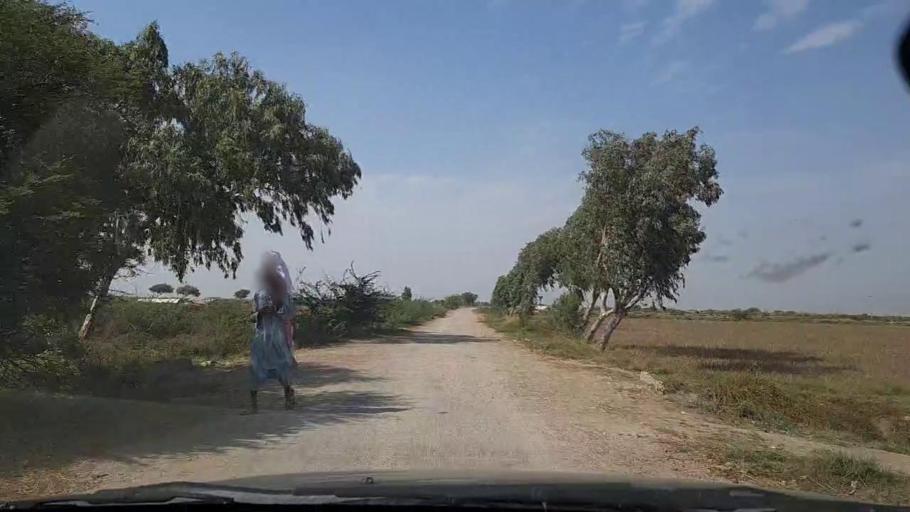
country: PK
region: Sindh
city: Mirpur Batoro
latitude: 24.5935
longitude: 68.2079
